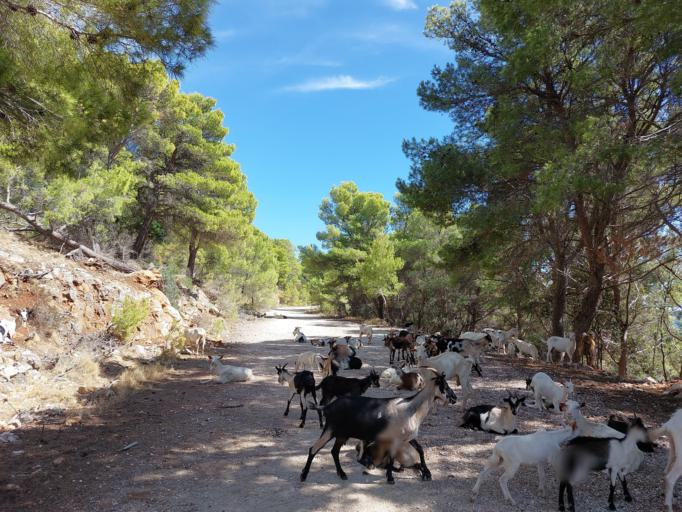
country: HR
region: Dubrovacko-Neretvanska
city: Smokvica
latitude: 42.7358
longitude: 16.8331
